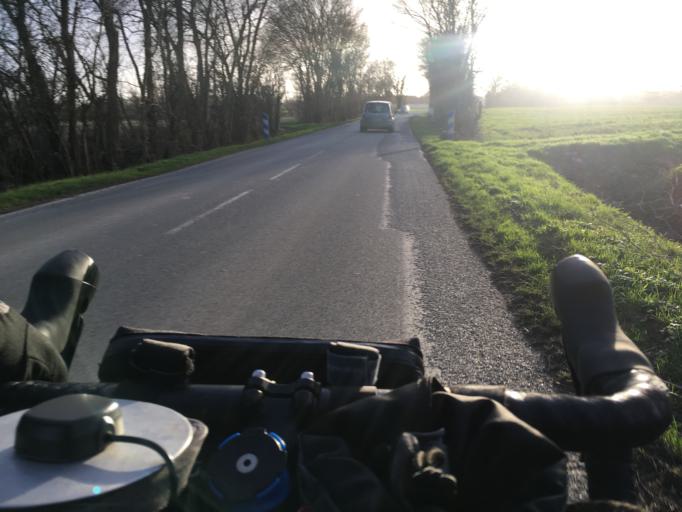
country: FR
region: Poitou-Charentes
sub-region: Departement de la Charente-Maritime
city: Courcon
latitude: 46.1672
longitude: -0.8529
